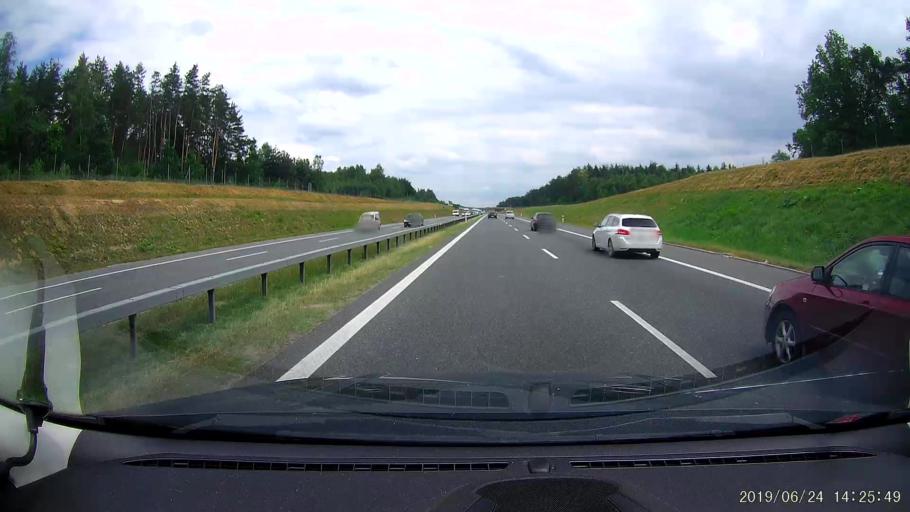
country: PL
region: Lesser Poland Voivodeship
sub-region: Powiat brzeski
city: Przyborow
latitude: 50.0004
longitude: 20.6350
